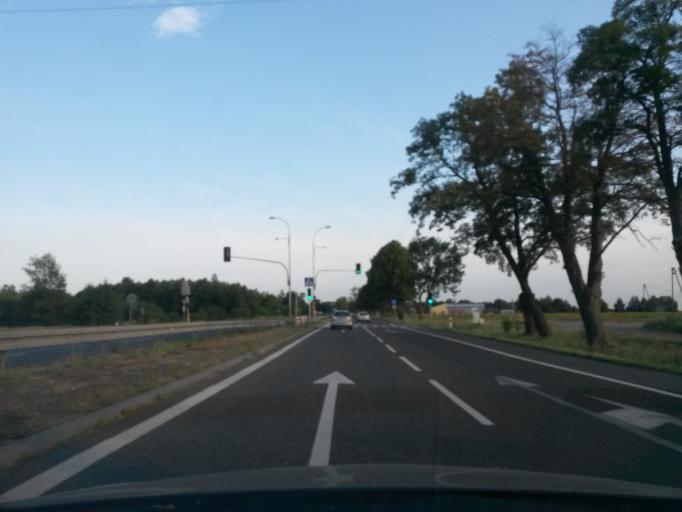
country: PL
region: Masovian Voivodeship
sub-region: Powiat plonski
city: Zaluski
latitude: 52.4878
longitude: 20.5481
